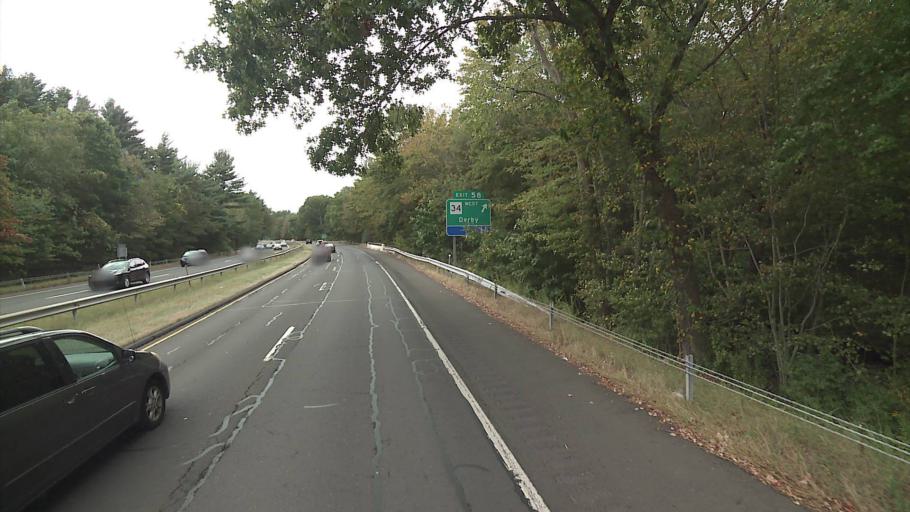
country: US
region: Connecticut
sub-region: New Haven County
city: Orange
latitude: 41.3099
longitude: -73.0316
